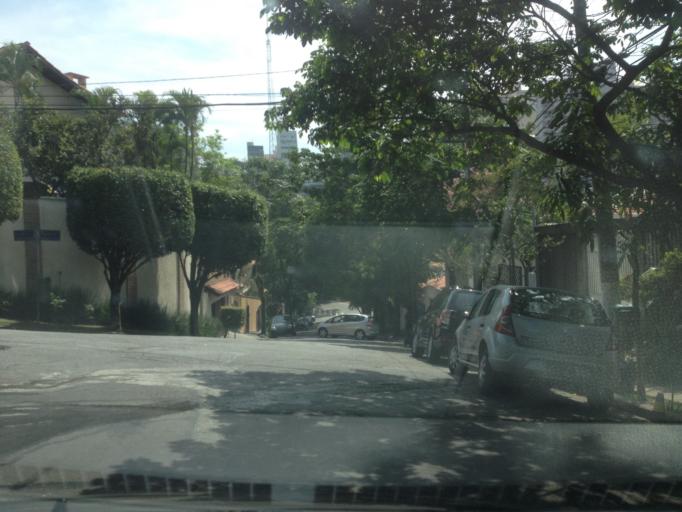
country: BR
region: Sao Paulo
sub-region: Sao Paulo
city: Sao Paulo
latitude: -23.5446
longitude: -46.6982
